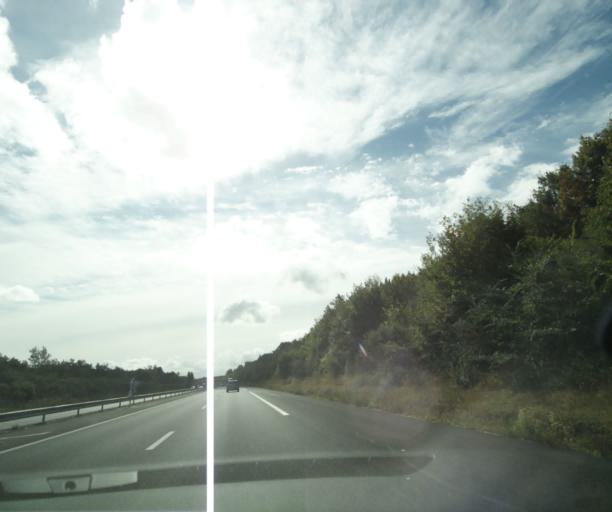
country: FR
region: Poitou-Charentes
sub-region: Departement de la Charente-Maritime
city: Thenac
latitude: 45.6417
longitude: -0.6275
